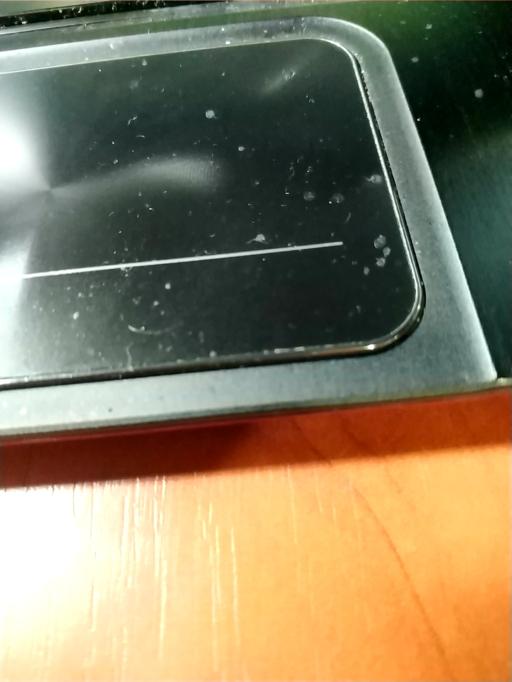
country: RU
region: Rjazan
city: Skopin
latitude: 53.9368
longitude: 39.5221
